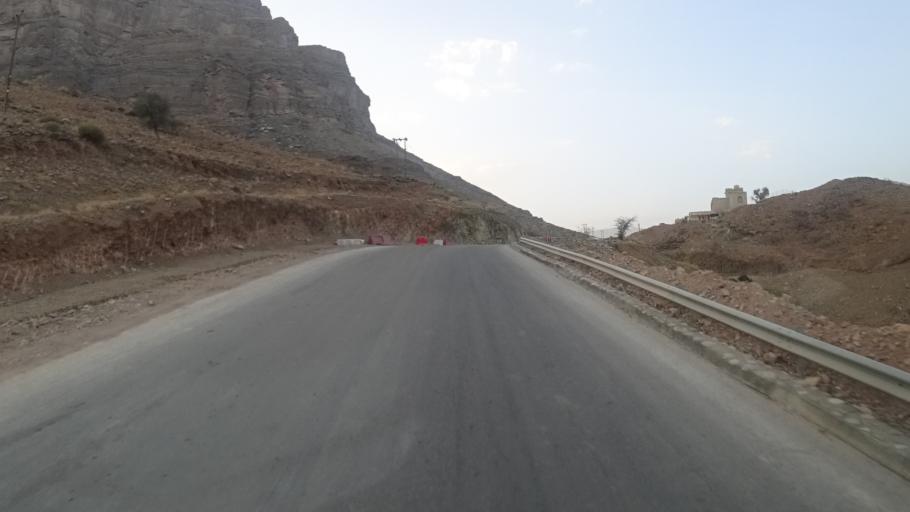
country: OM
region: Muhafazat ad Dakhiliyah
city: Bahla'
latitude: 23.2129
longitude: 57.1466
